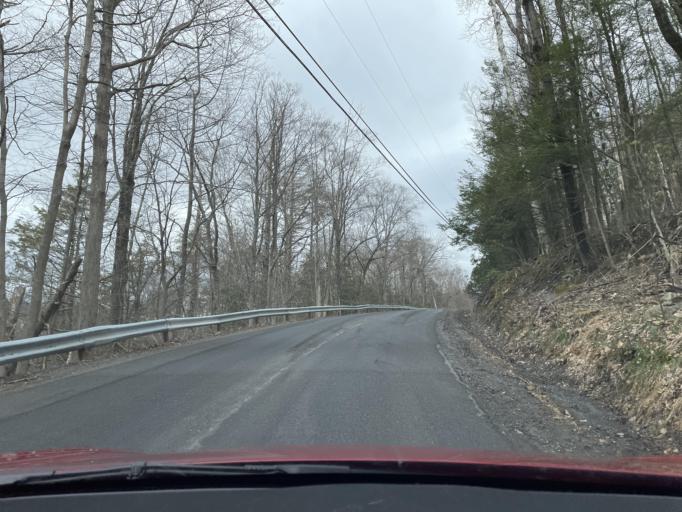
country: US
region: New York
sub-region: Ulster County
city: Woodstock
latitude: 42.0747
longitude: -74.1481
